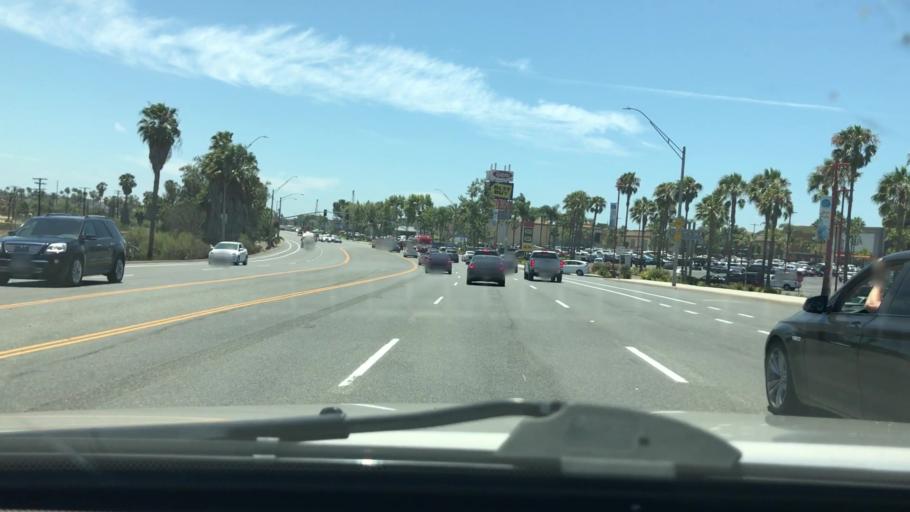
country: US
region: California
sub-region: Orange County
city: Seal Beach
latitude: 33.7624
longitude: -118.1149
